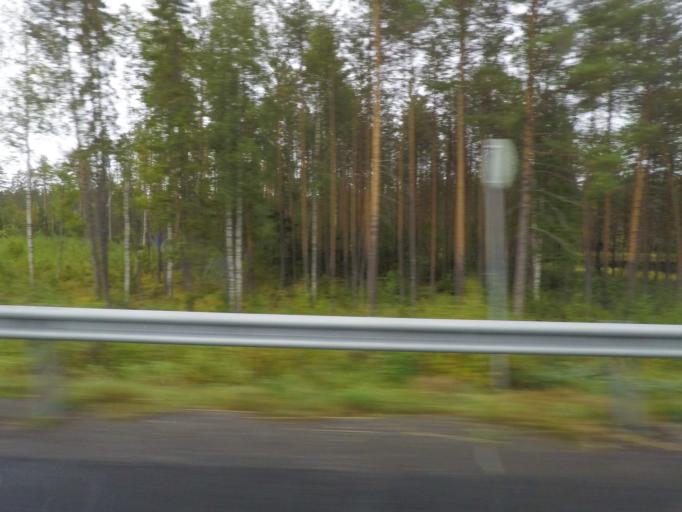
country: FI
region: Northern Savo
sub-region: Varkaus
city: Leppaevirta
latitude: 62.5014
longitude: 27.7329
